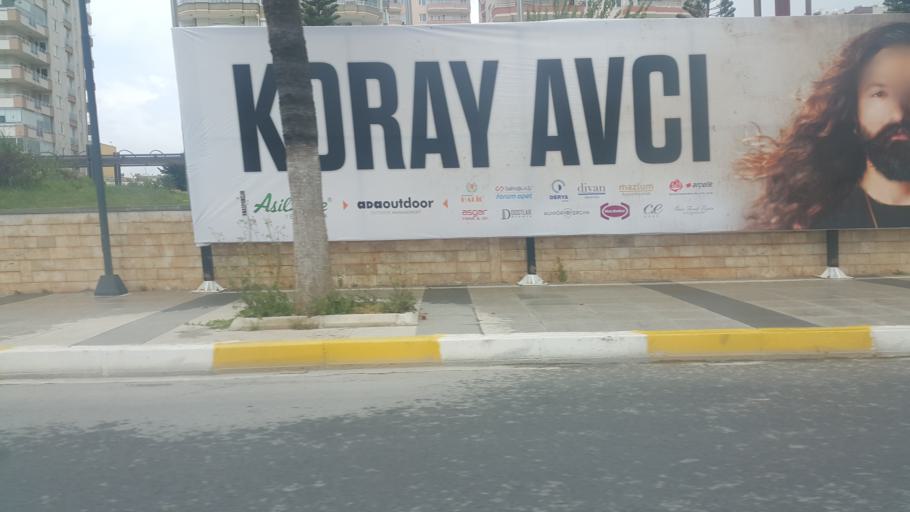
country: TR
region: Mersin
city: Mercin
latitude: 36.7726
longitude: 34.5690
